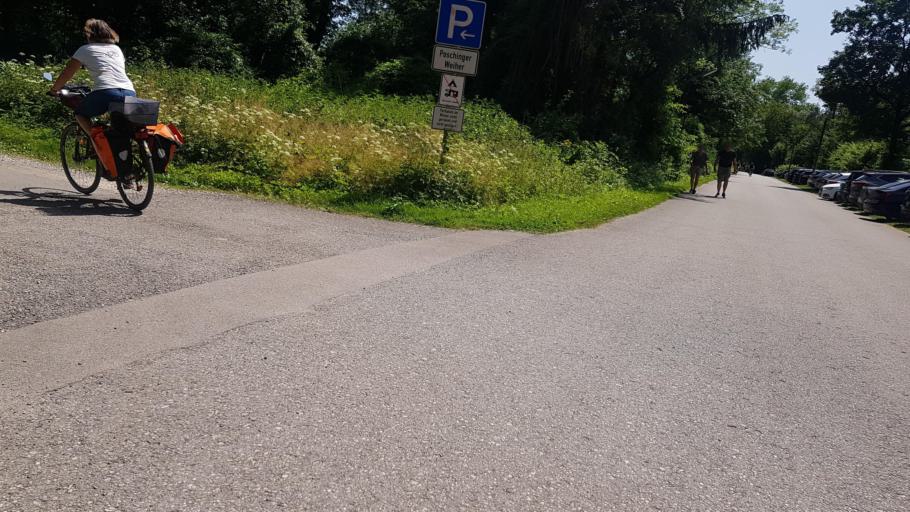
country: DE
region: Bavaria
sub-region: Upper Bavaria
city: Unterfoehring
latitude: 48.2028
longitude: 11.6427
